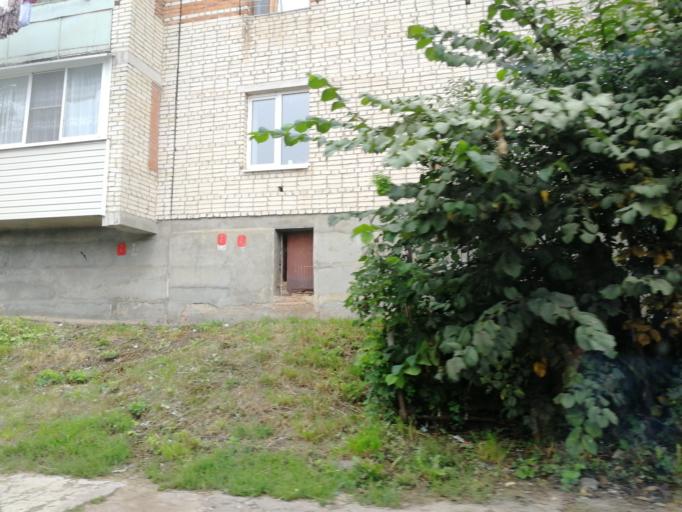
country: RU
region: Tula
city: Bogoroditsk
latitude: 53.7675
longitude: 38.1273
